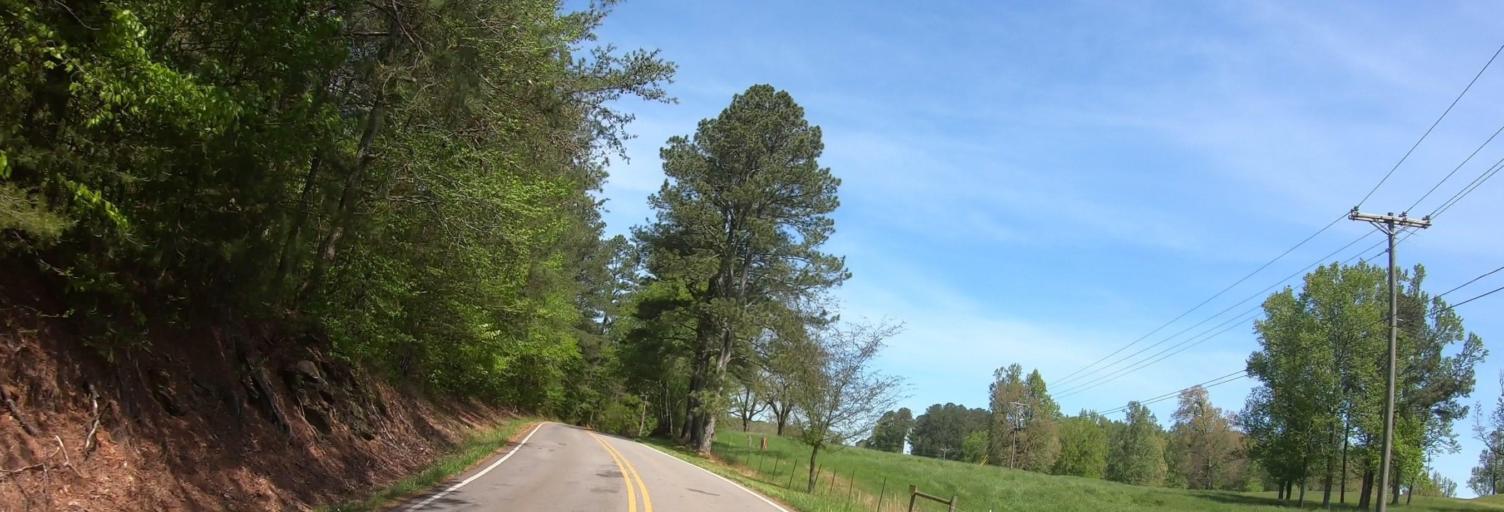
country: US
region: Georgia
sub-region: Bartow County
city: Rydal
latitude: 34.3943
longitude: -84.5925
